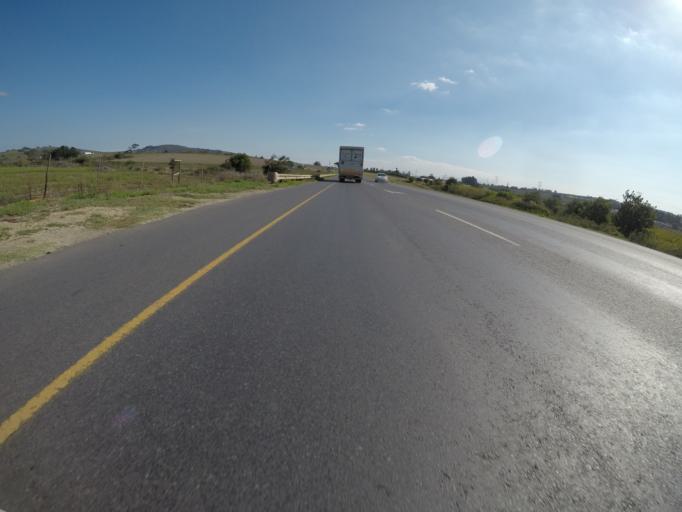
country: ZA
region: Western Cape
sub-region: City of Cape Town
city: Kraaifontein
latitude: -33.8895
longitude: 18.7433
